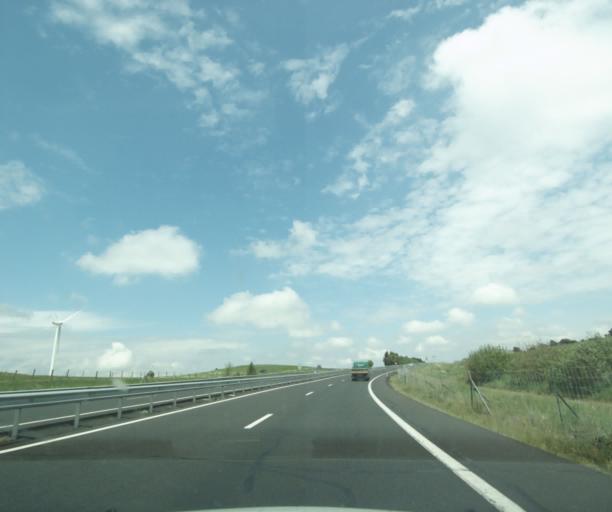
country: FR
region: Auvergne
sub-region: Departement du Cantal
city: Saint-Flour
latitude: 45.1045
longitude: 3.1297
